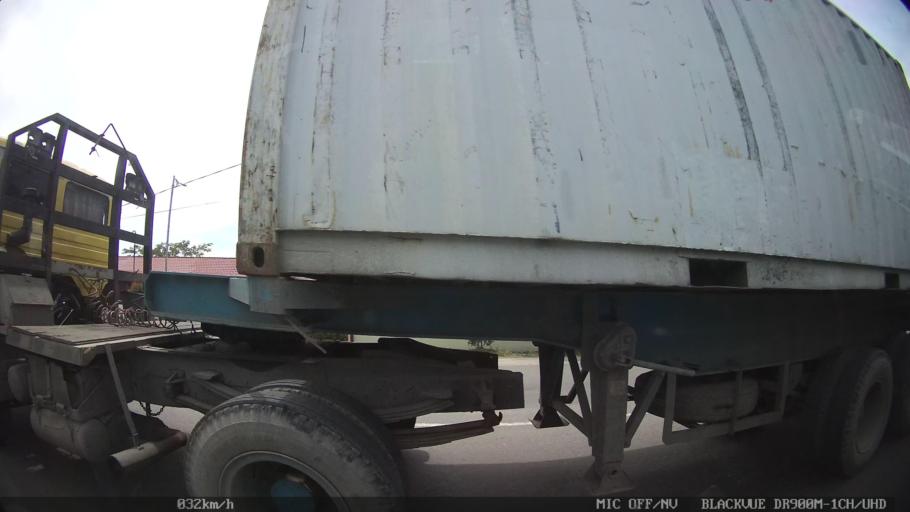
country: ID
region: North Sumatra
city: Belawan
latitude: 3.7773
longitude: 98.7022
